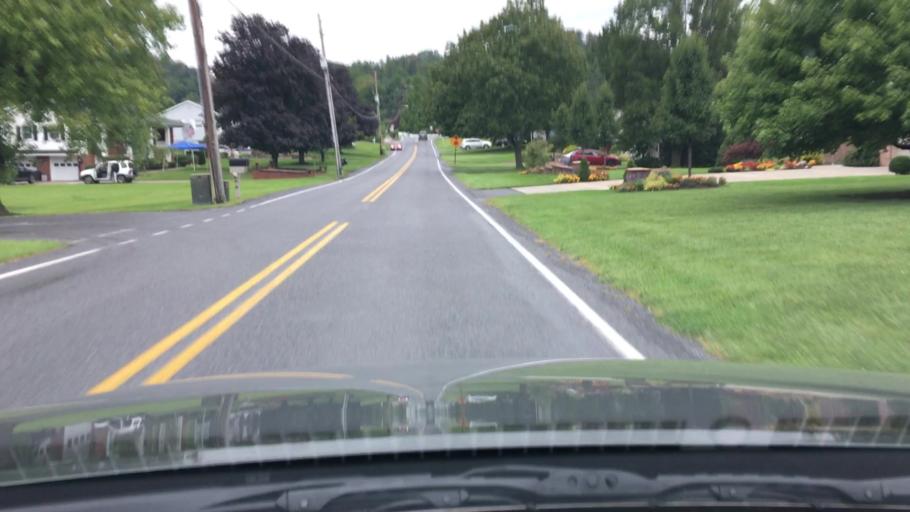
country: US
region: Pennsylvania
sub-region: Blair County
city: Duncansville
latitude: 40.4163
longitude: -78.4168
